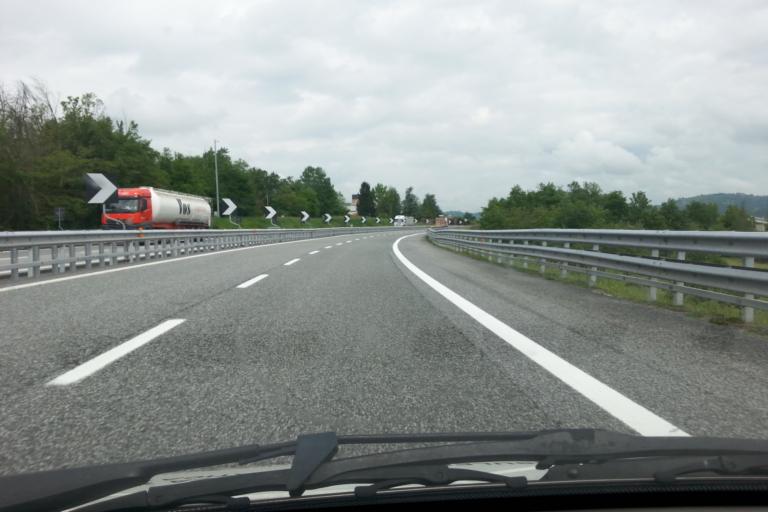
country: IT
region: Piedmont
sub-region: Provincia di Cuneo
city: Lesegno
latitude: 44.3976
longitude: 7.9780
